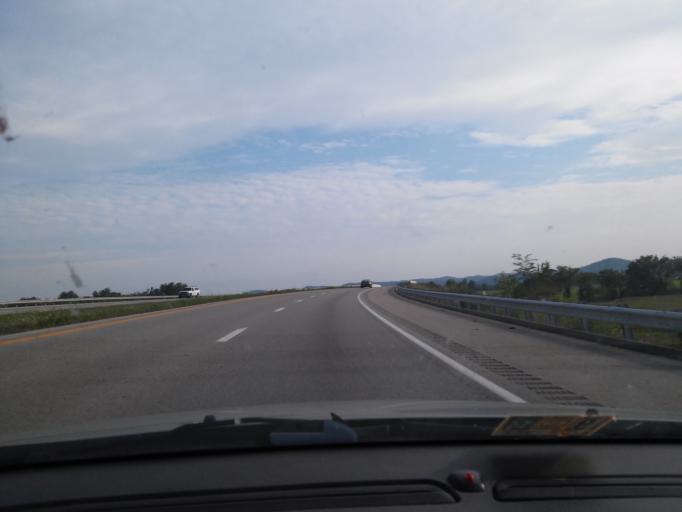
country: US
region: Ohio
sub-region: Ross County
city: Chillicothe
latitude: 39.2783
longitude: -82.8838
